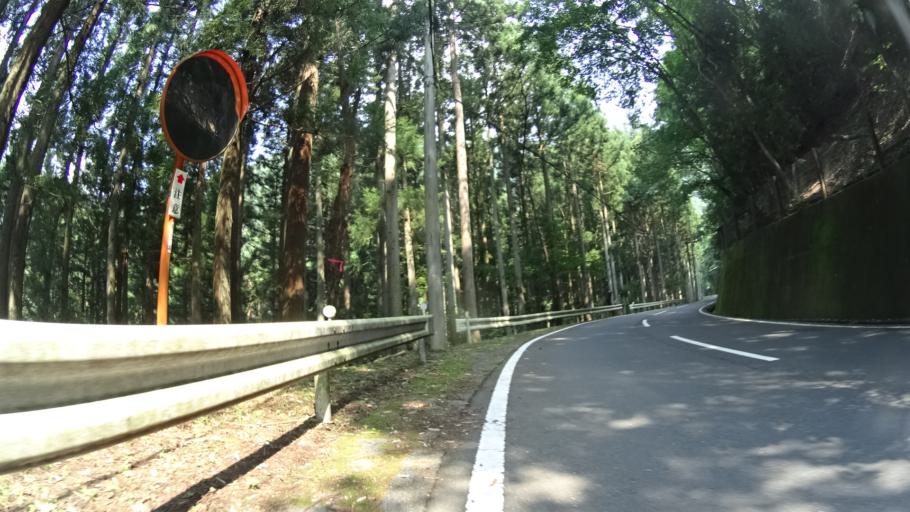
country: JP
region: Gunma
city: Tomioka
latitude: 36.0611
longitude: 138.8531
